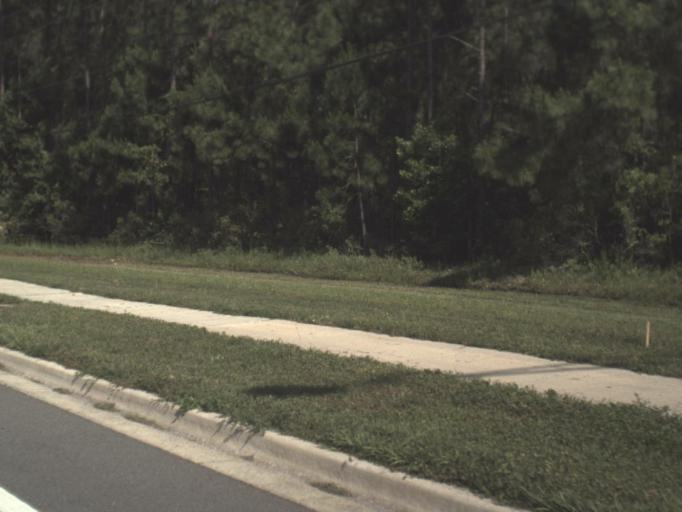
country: US
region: Florida
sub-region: Duval County
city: Neptune Beach
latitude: 30.2875
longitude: -81.4851
